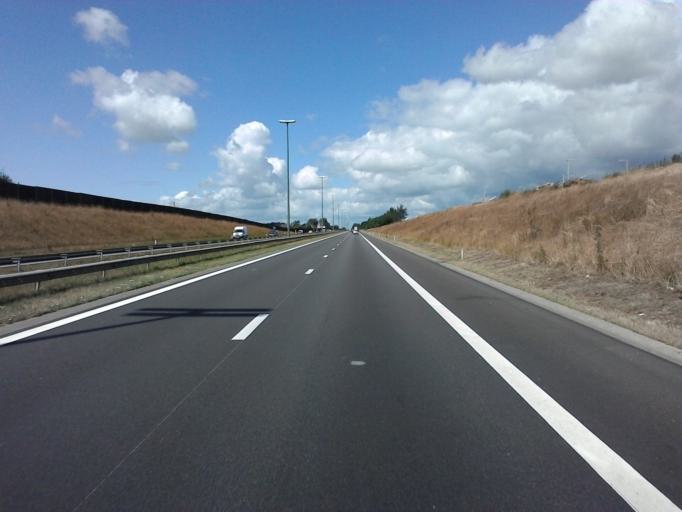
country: BE
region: Wallonia
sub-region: Province du Luxembourg
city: Attert
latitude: 49.6936
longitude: 5.7115
